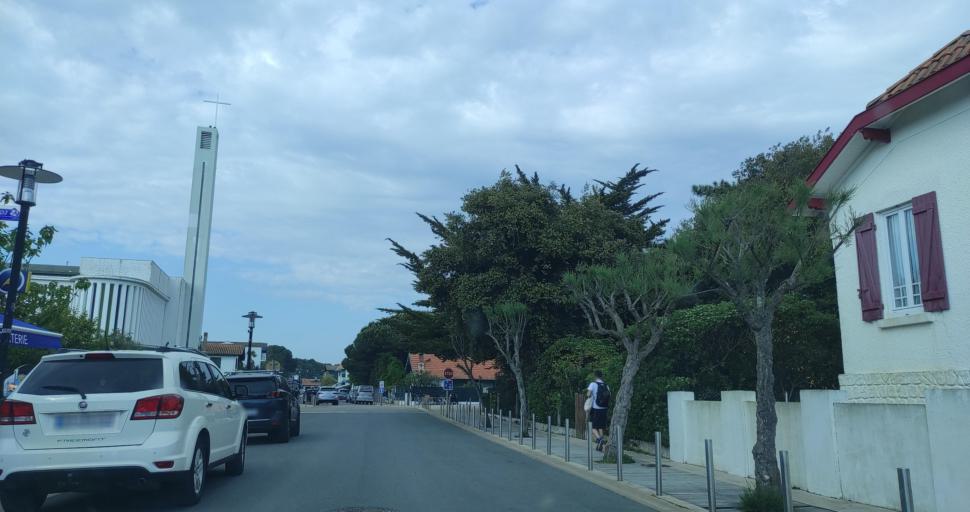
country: FR
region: Aquitaine
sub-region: Departement de la Gironde
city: Arcachon
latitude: 44.6535
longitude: -1.2417
